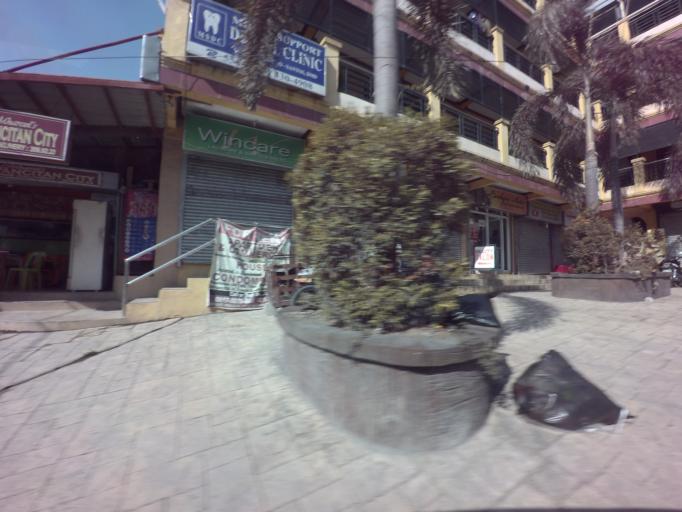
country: PH
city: Sambayanihan People's Village
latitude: 14.4645
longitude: 121.0170
